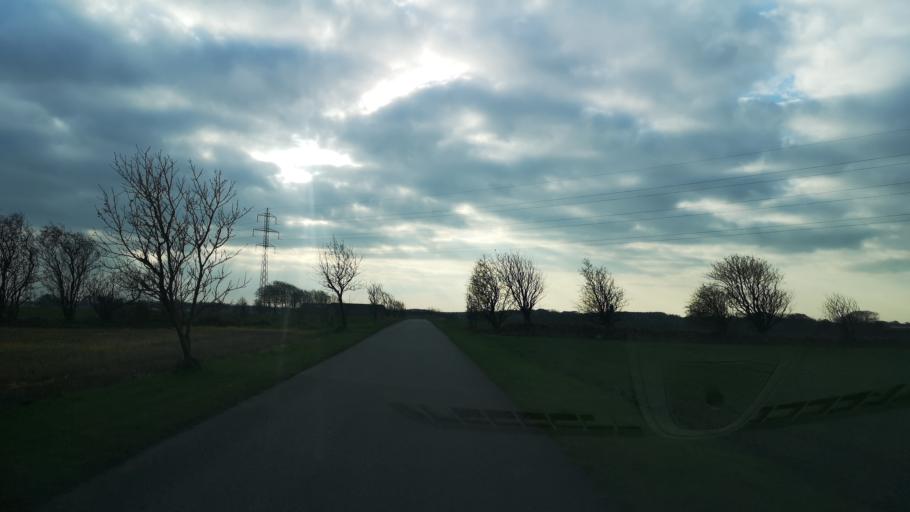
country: DK
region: Central Jutland
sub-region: Ringkobing-Skjern Kommune
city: Videbaek
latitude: 56.0011
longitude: 8.5897
